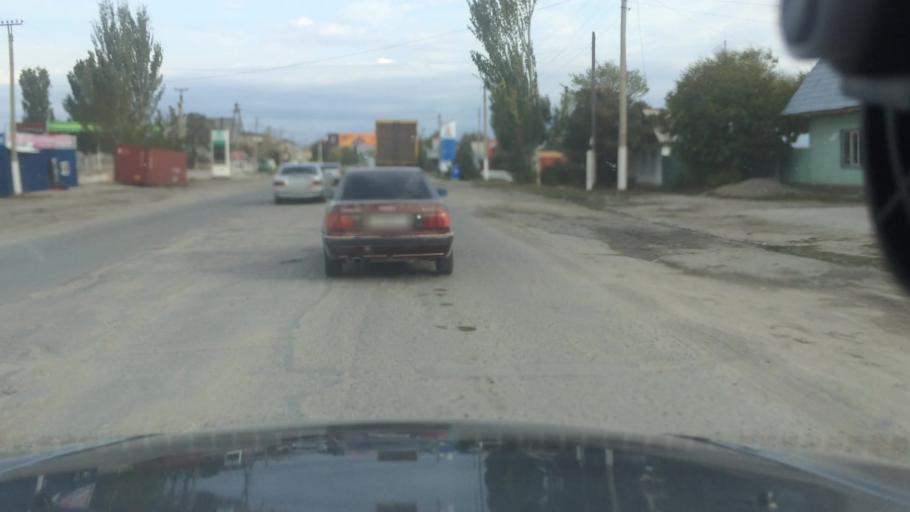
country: KG
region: Ysyk-Koel
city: Karakol
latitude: 42.5119
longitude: 78.3857
